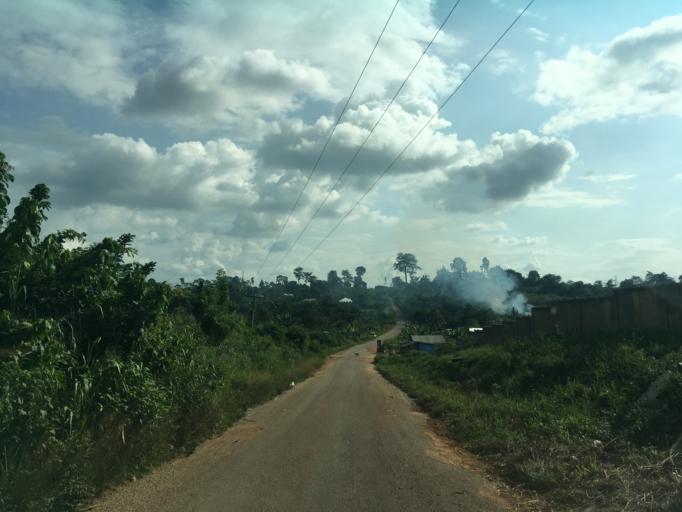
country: GH
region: Western
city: Bibiani
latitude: 6.7962
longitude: -2.5275
